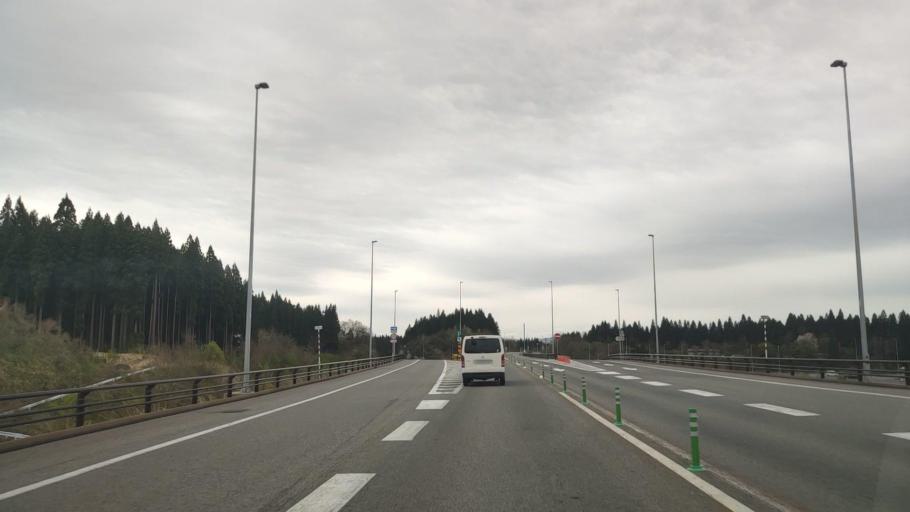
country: JP
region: Akita
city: Odate
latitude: 40.3133
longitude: 140.5793
